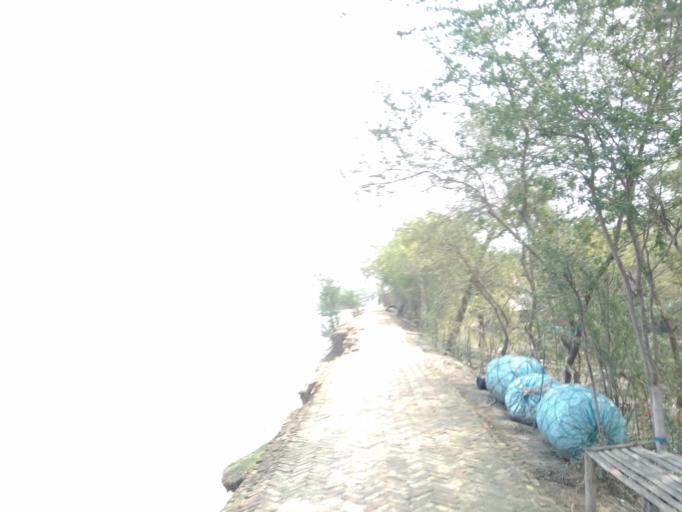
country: IN
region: West Bengal
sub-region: North 24 Parganas
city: Taki
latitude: 22.2811
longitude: 89.2868
